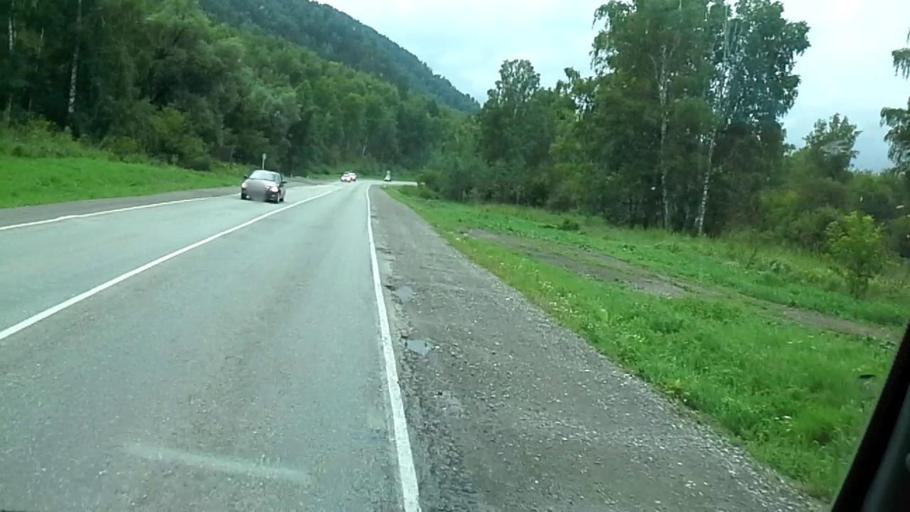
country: RU
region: Altay
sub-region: Mayminskiy Rayon
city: Manzherok
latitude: 51.8613
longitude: 85.7601
